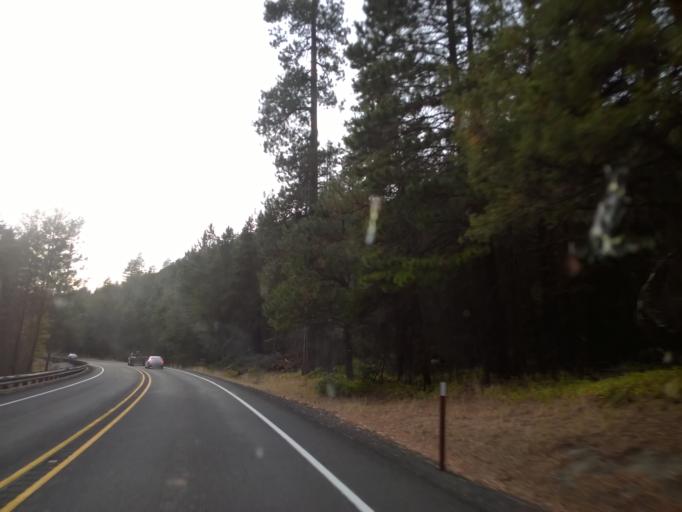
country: US
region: Washington
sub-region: Chelan County
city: Cashmere
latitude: 47.3350
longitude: -120.6284
